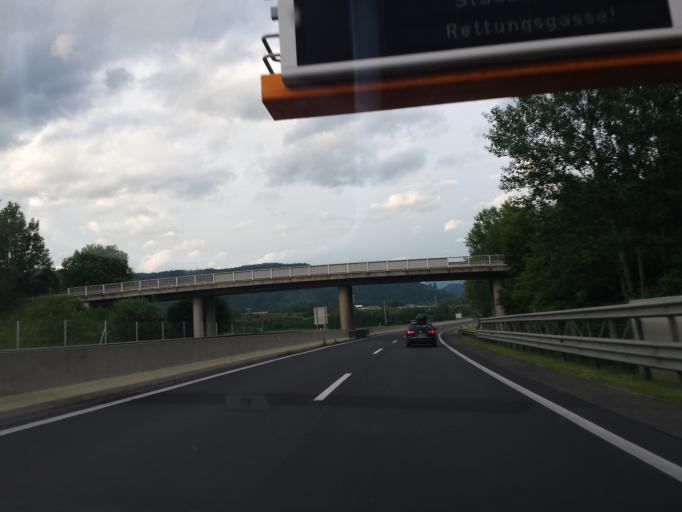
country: AT
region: Styria
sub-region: Politischer Bezirk Leoben
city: Sankt Michael in Obersteiermark
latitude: 47.3364
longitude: 14.9956
